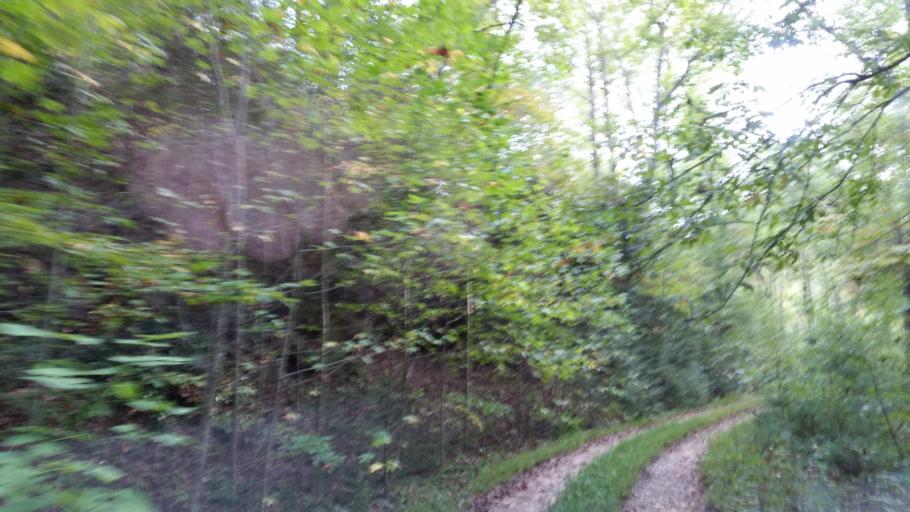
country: US
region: Georgia
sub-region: Dawson County
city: Dawsonville
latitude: 34.5803
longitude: -84.1767
